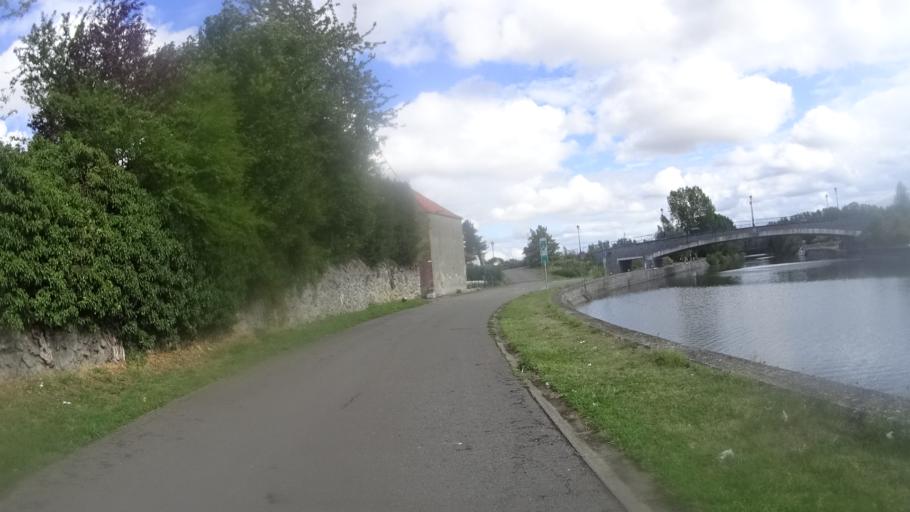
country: BE
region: Wallonia
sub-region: Province du Hainaut
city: Merbes-le-Chateau
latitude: 50.3230
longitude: 4.1632
